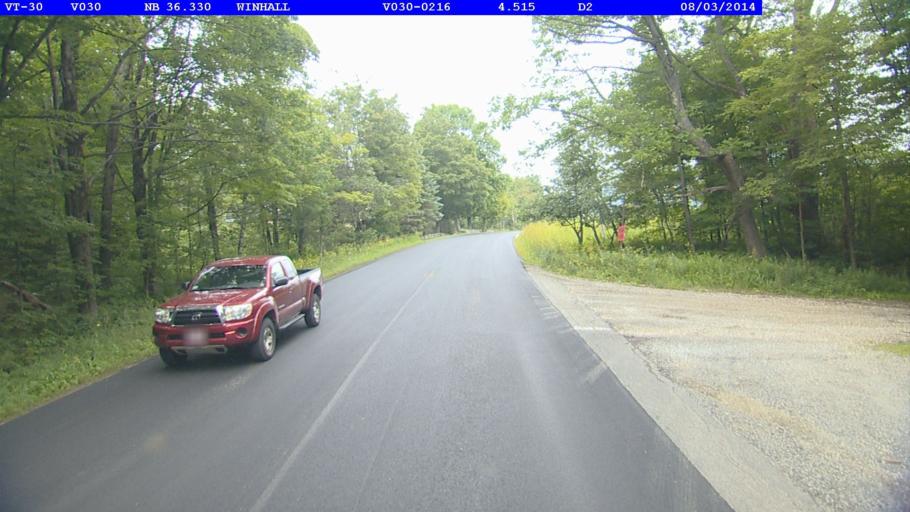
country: US
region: Vermont
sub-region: Bennington County
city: Manchester Center
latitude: 43.1746
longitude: -72.9249
